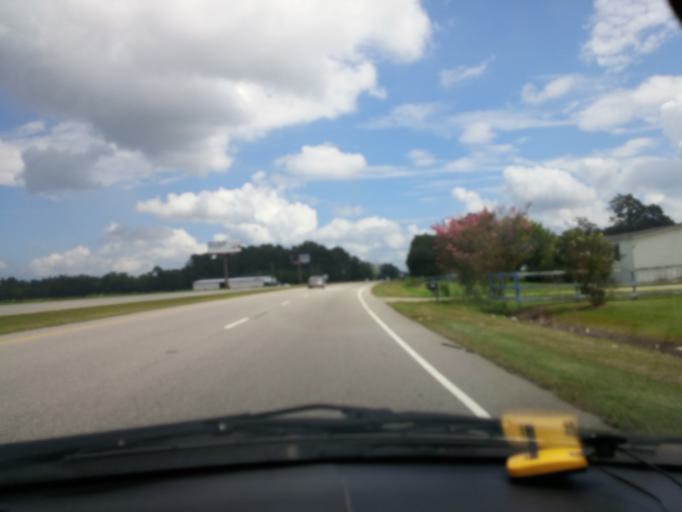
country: US
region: North Carolina
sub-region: Pitt County
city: Grifton
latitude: 35.3218
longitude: -77.5102
